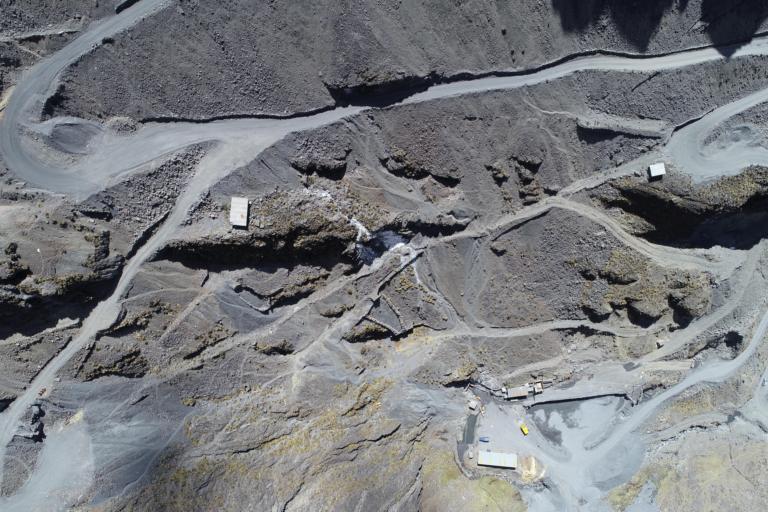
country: BO
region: La Paz
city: Sorata
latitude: -15.6699
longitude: -68.5617
